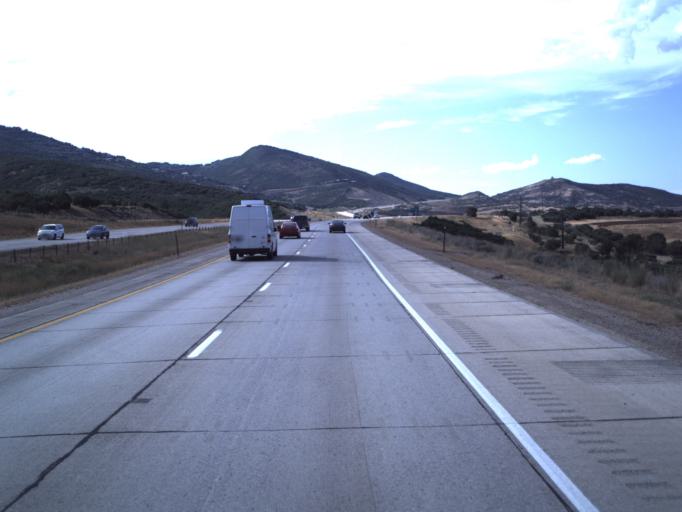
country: US
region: Utah
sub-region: Summit County
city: Park City
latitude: 40.6168
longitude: -111.4346
